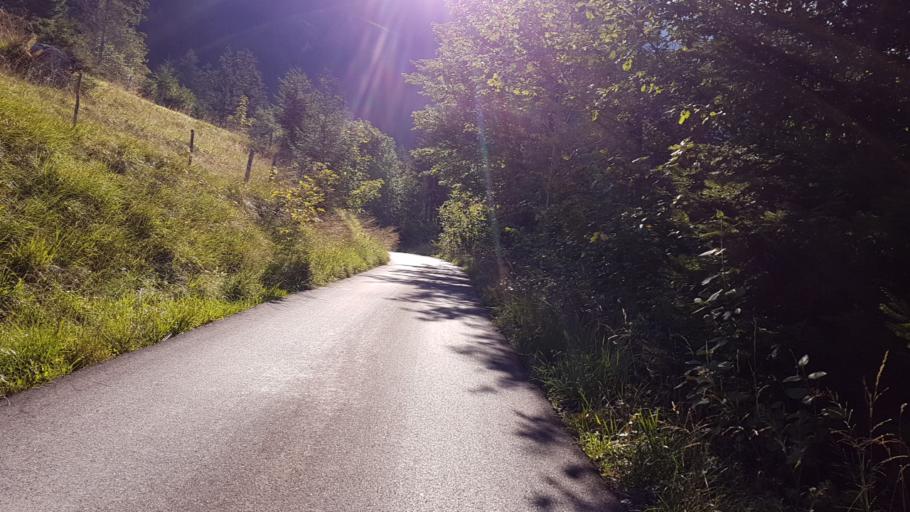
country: CH
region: Bern
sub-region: Frutigen-Niedersimmental District
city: Frutigen
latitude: 46.5520
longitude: 7.6712
